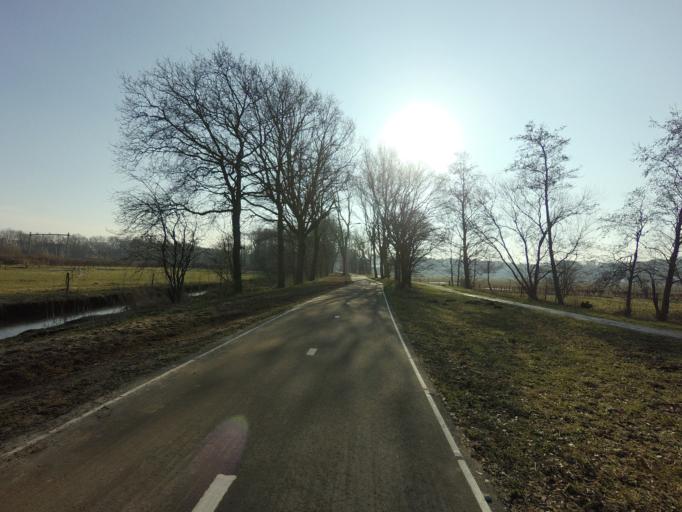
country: NL
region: North Holland
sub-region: Gemeente Velsen
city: Velsen-Zuid
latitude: 52.4375
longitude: 4.6323
